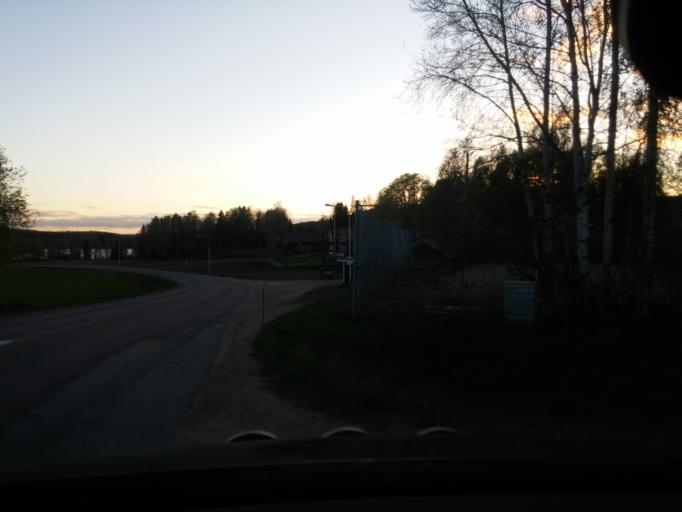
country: SE
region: Gaevleborg
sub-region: Bollnas Kommun
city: Bollnas
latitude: 61.4075
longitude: 16.5439
